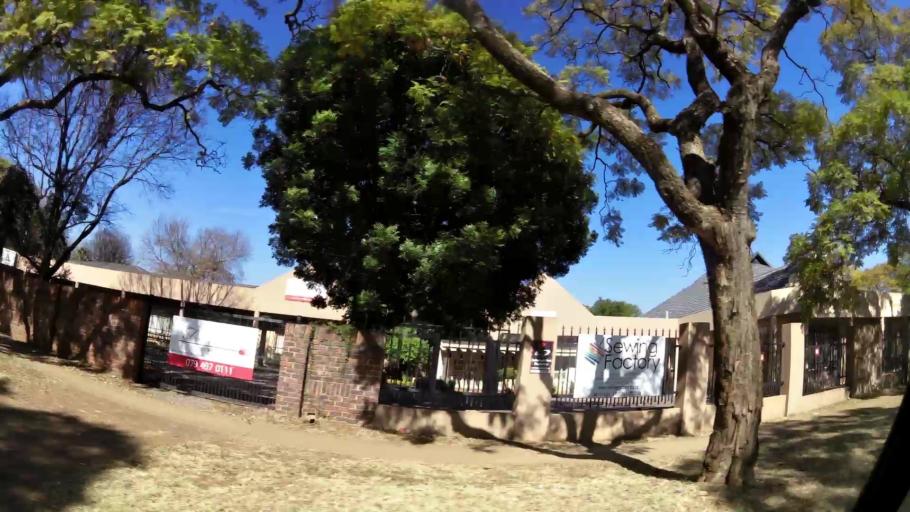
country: ZA
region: Gauteng
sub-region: City of Tshwane Metropolitan Municipality
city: Pretoria
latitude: -25.7683
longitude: 28.2412
